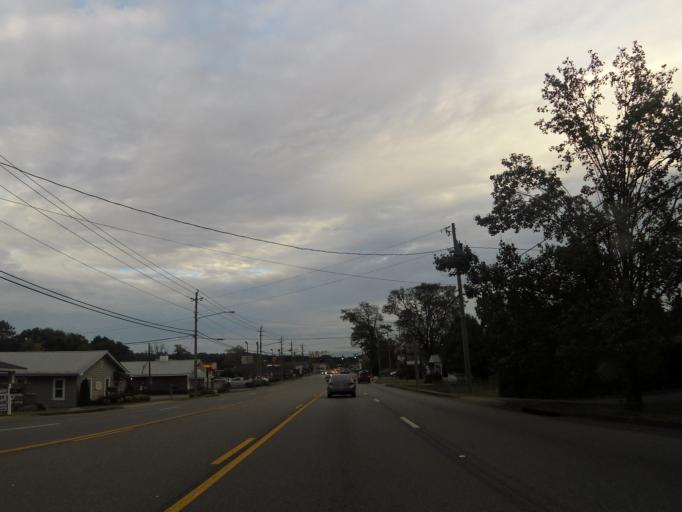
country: US
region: Alabama
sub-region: Jefferson County
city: Trussville
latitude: 33.6179
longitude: -86.6138
